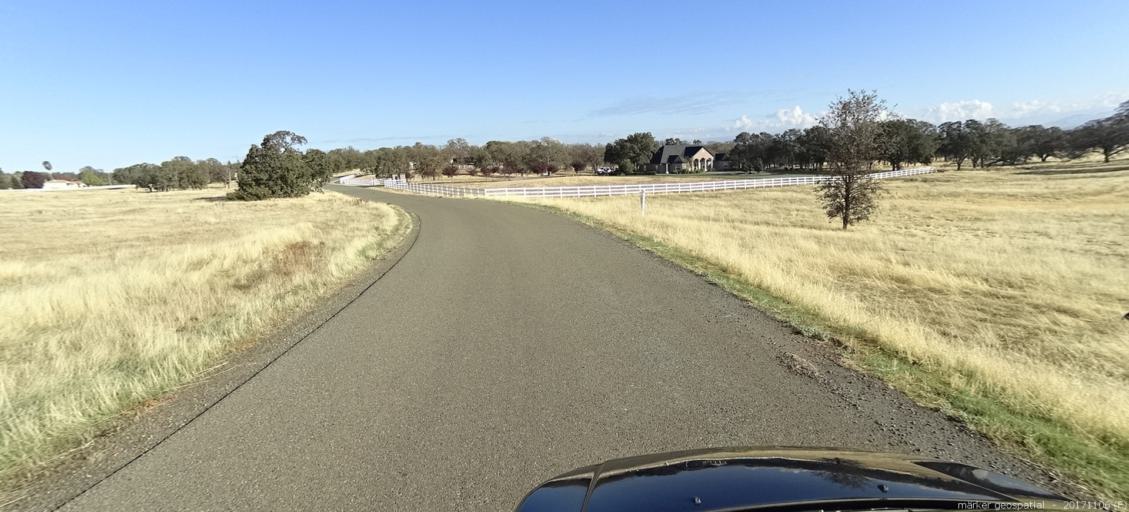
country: US
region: California
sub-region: Shasta County
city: Palo Cedro
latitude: 40.4991
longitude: -122.2454
